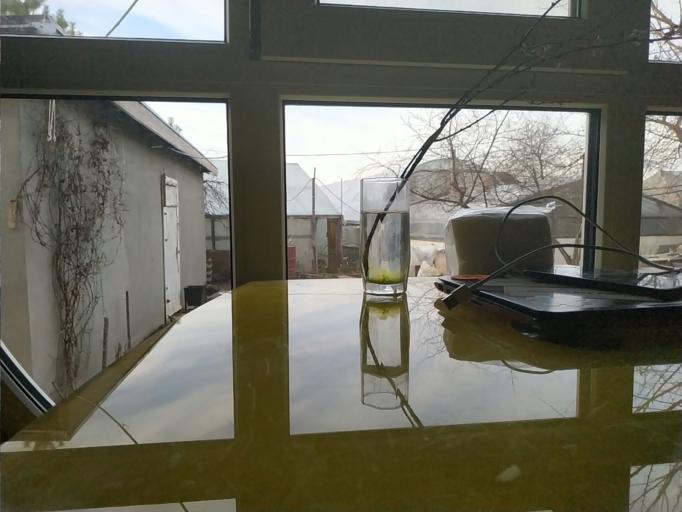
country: RU
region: Republic of Karelia
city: Suoyarvi
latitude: 61.8720
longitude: 32.2682
